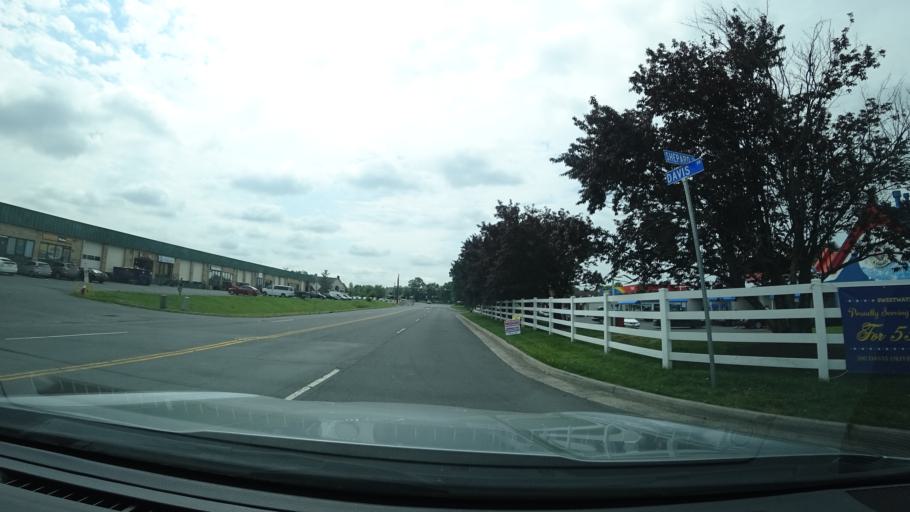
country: US
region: Virginia
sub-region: Loudoun County
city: Sterling
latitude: 38.9936
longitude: -77.4211
